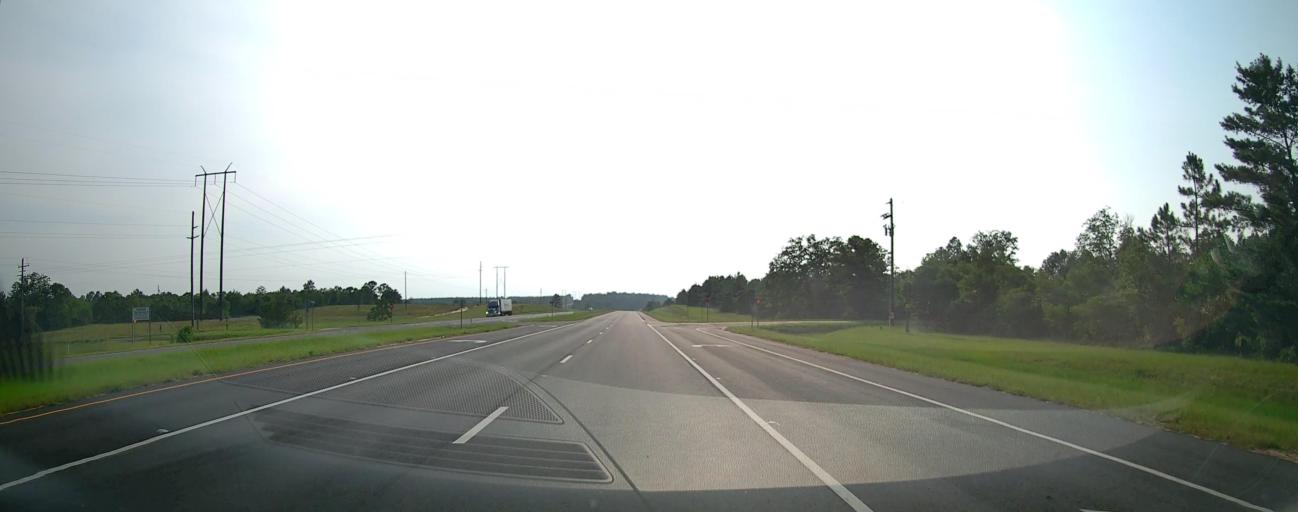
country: US
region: Georgia
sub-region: Taylor County
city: Butler
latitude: 32.5927
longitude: -84.3851
